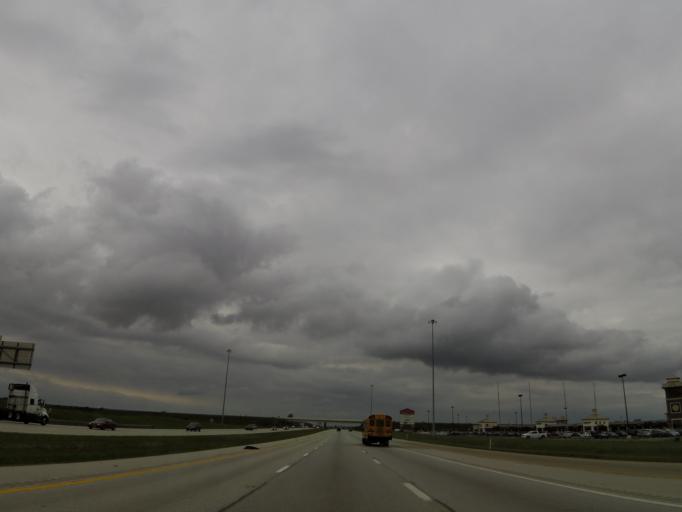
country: US
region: Ohio
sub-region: Fayette County
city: Jeffersonville
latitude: 39.6209
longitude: -83.6047
